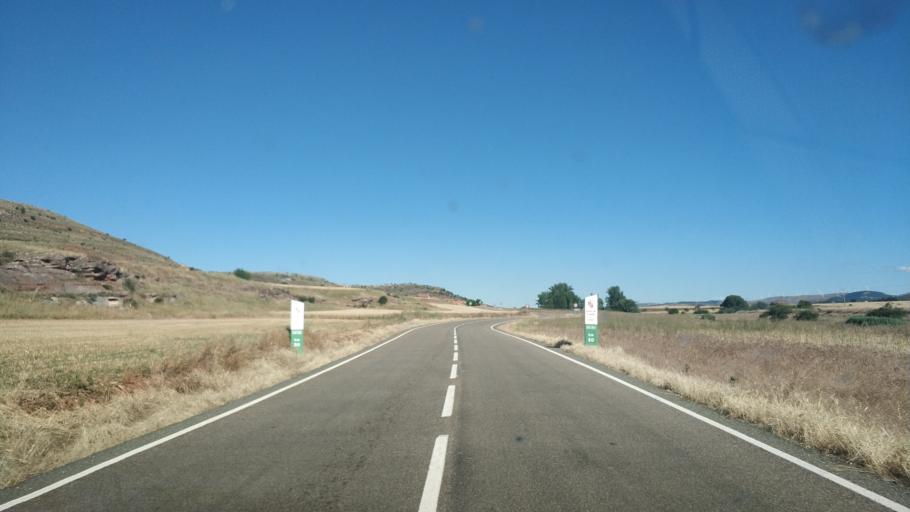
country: ES
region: Castille and Leon
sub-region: Provincia de Soria
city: Montejo de Tiermes
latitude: 41.3640
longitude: -3.1891
